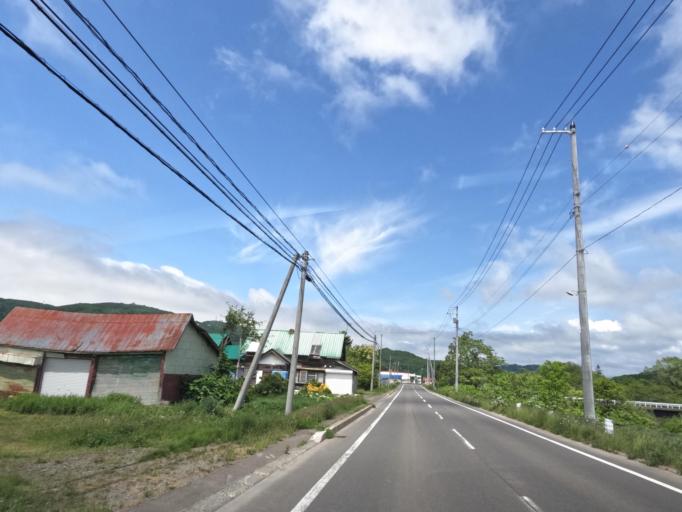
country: JP
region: Hokkaido
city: Tobetsu
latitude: 43.2824
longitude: 141.5363
